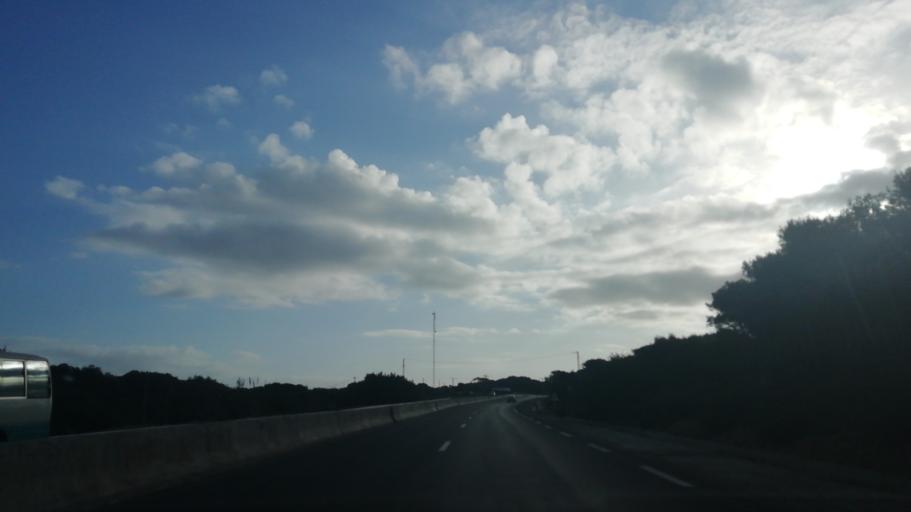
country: DZ
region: Mostaganem
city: Mostaganem
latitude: 36.1132
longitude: 0.2322
